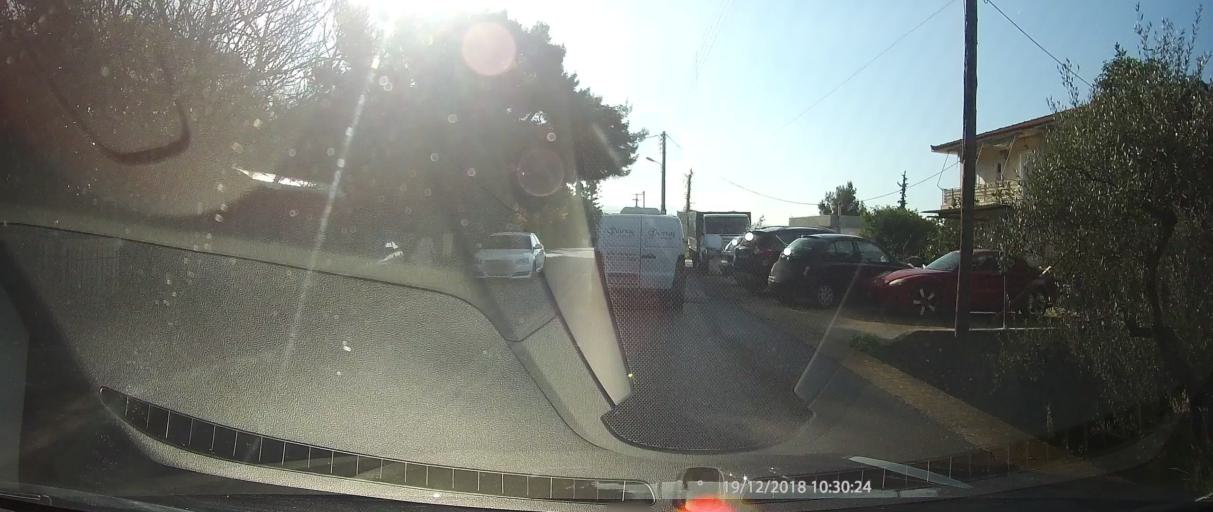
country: GR
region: Peloponnese
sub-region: Nomos Messinias
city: Paralia Vergas
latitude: 37.0164
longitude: 22.1528
